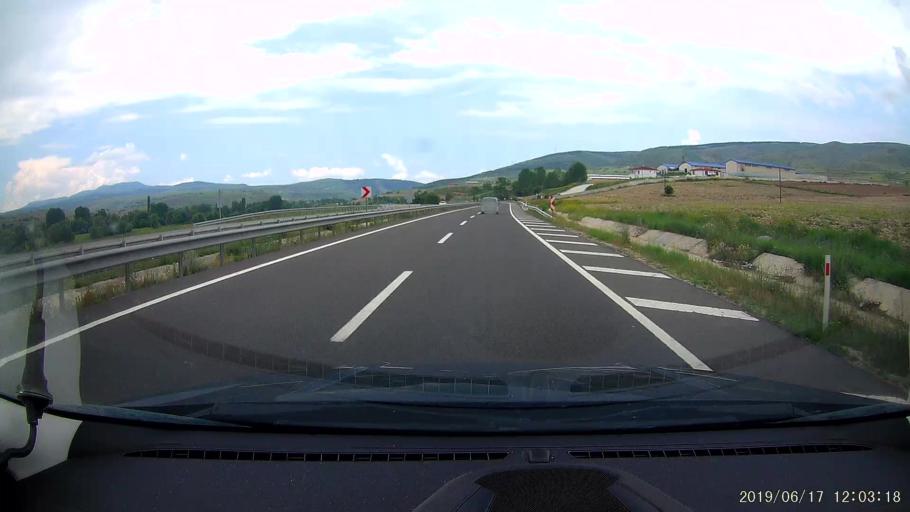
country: TR
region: Cankiri
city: Cerkes
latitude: 40.8251
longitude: 32.8263
